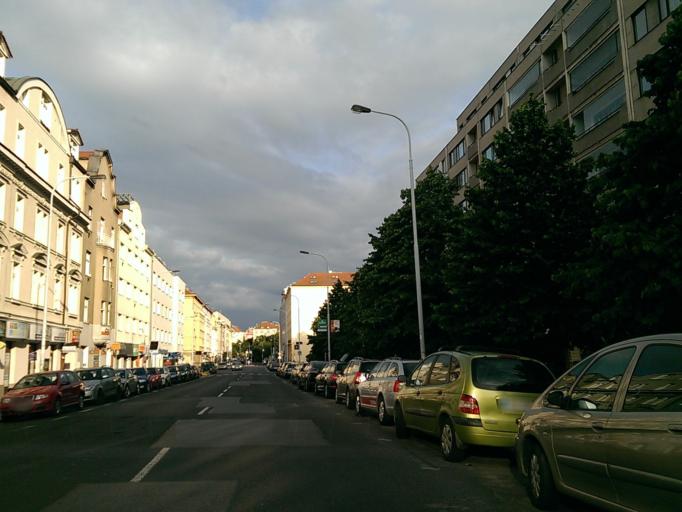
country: CZ
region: Praha
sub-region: Praha 2
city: Vysehrad
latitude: 50.0591
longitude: 14.4306
